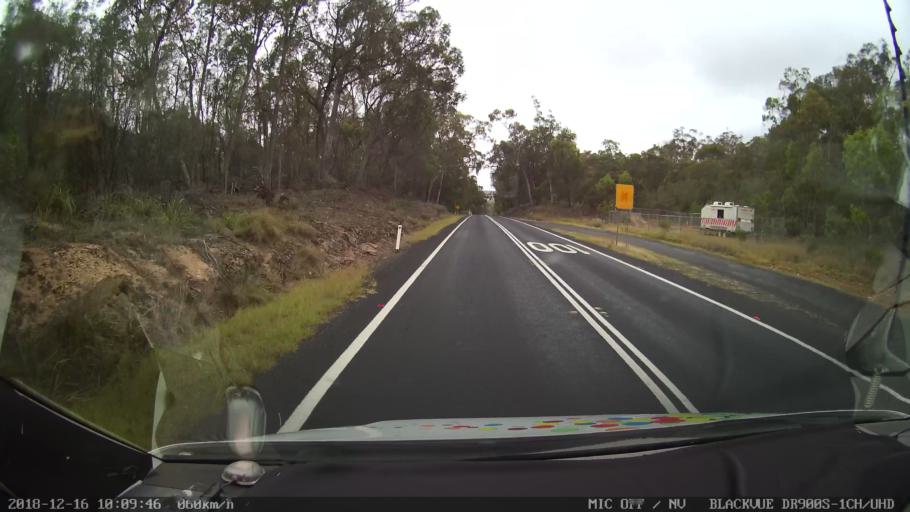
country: AU
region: New South Wales
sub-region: Glen Innes Severn
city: Glen Innes
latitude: -29.3221
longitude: 151.9186
